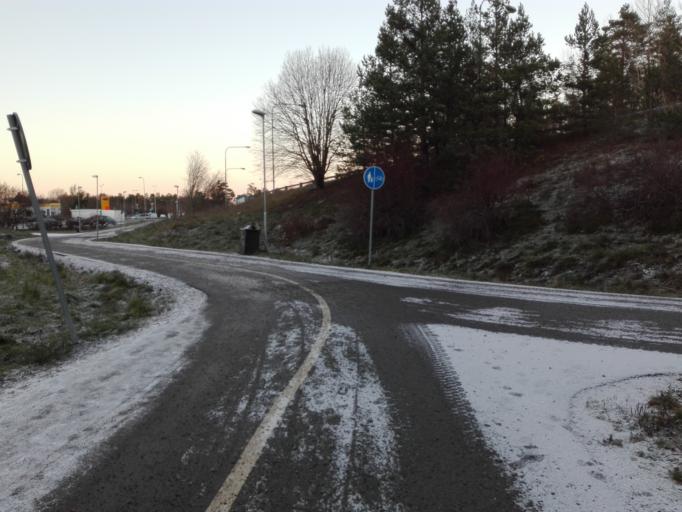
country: SE
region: Stockholm
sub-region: Nacka Kommun
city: Fisksatra
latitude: 59.2890
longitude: 18.2487
